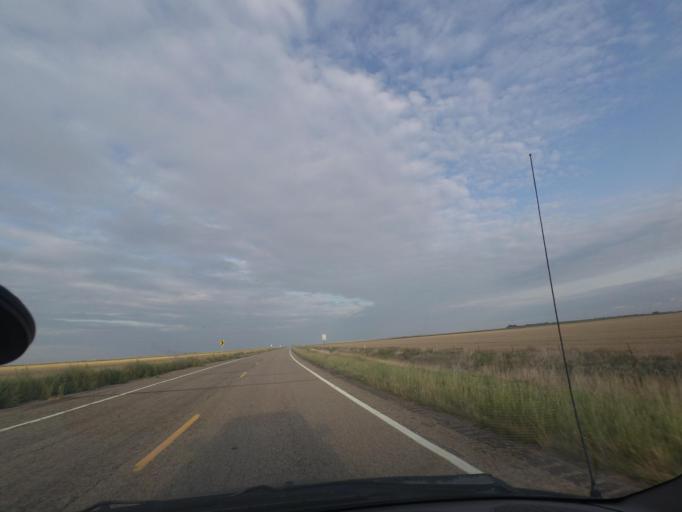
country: US
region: Colorado
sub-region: Yuma County
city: Wray
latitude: 39.7017
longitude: -102.3840
